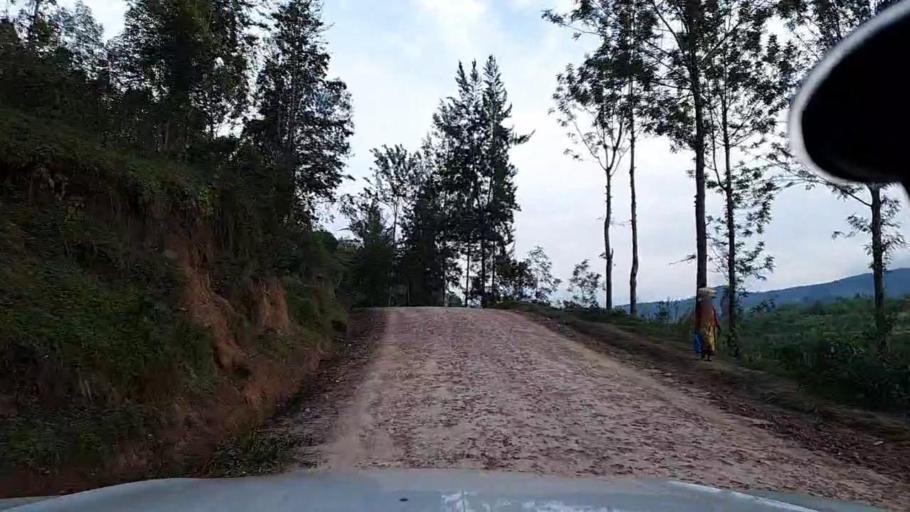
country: RW
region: Southern Province
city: Nyanza
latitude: -2.2170
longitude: 29.6433
